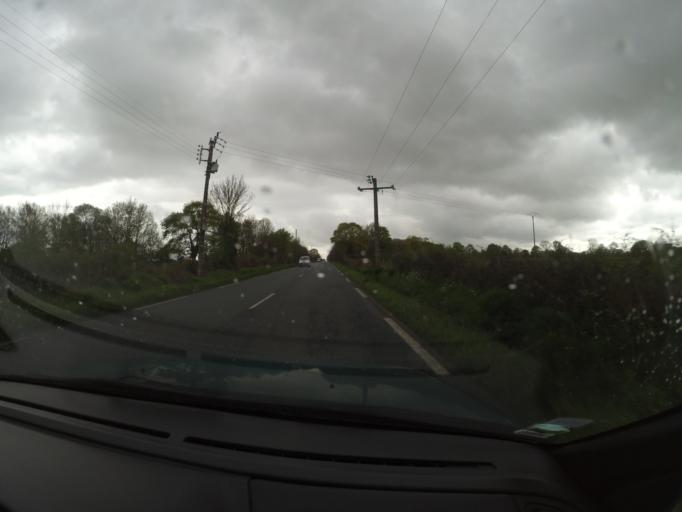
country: FR
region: Pays de la Loire
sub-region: Departement de la Loire-Atlantique
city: Vallet
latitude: 47.1873
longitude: -1.2544
